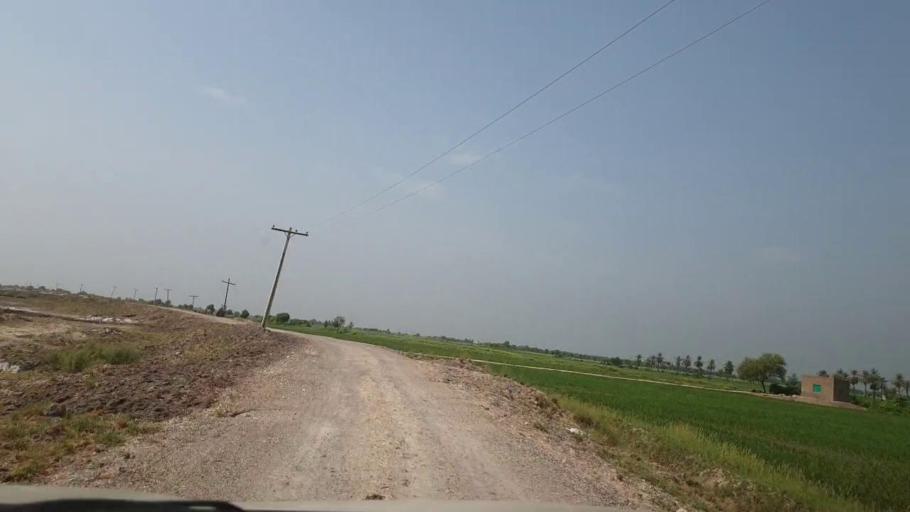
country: PK
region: Sindh
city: Dokri
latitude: 27.4265
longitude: 68.2042
